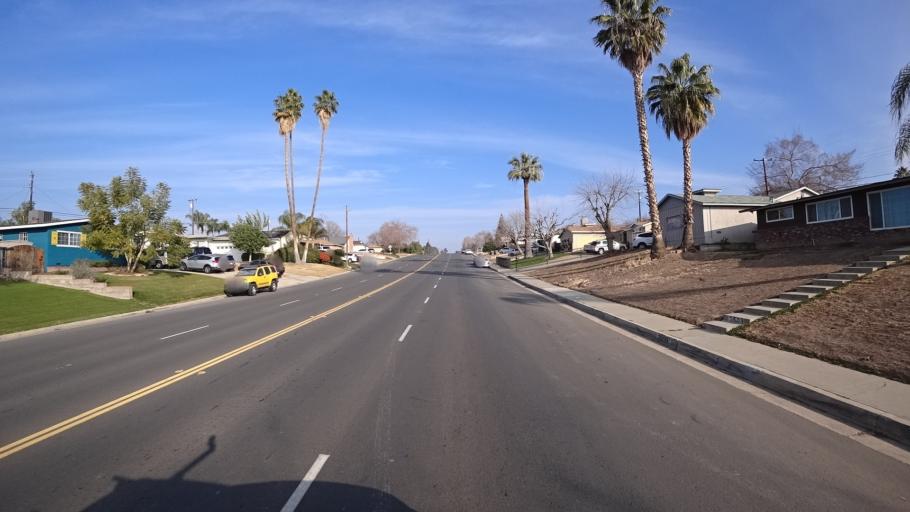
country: US
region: California
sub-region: Kern County
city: Oildale
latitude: 35.3998
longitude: -118.9763
